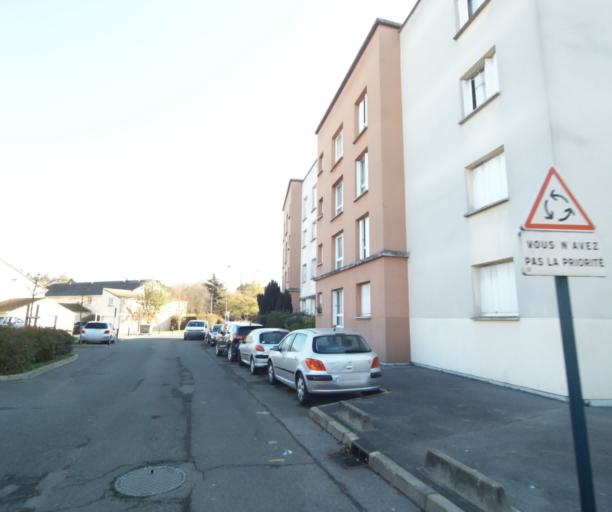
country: FR
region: Ile-de-France
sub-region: Departement du Val-d'Oise
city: Arnouville
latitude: 48.9921
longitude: 2.4315
